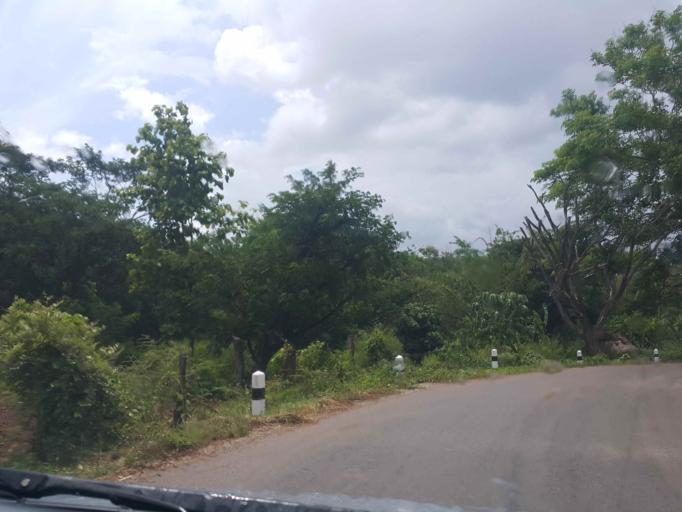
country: TH
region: Phayao
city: Dok Kham Tai
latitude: 19.0635
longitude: 100.0268
